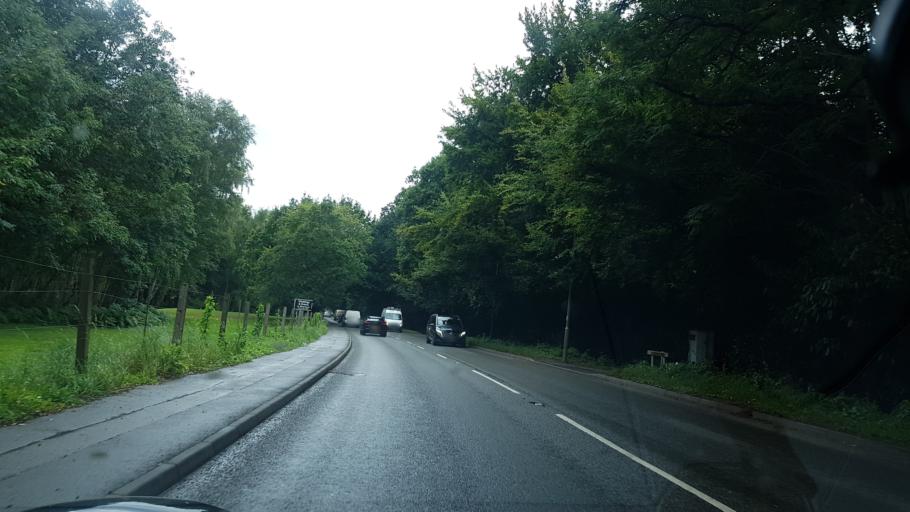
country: GB
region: England
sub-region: Surrey
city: Byfleet
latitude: 51.3400
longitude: -0.4547
